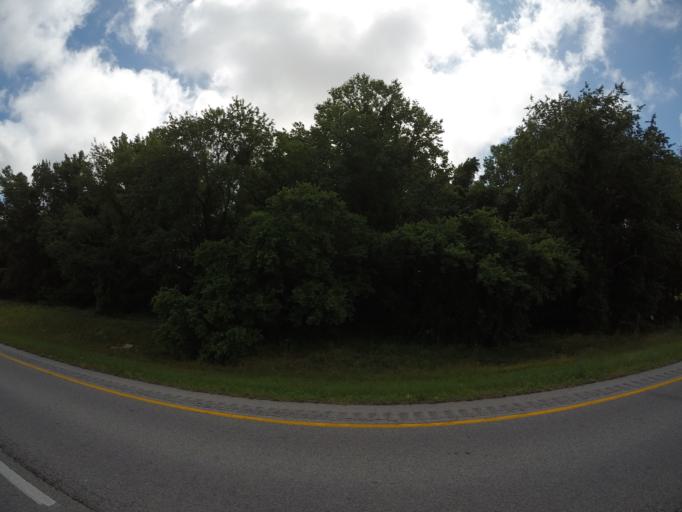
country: US
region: Maryland
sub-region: Queen Anne's County
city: Centreville
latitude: 39.0951
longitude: -75.9635
